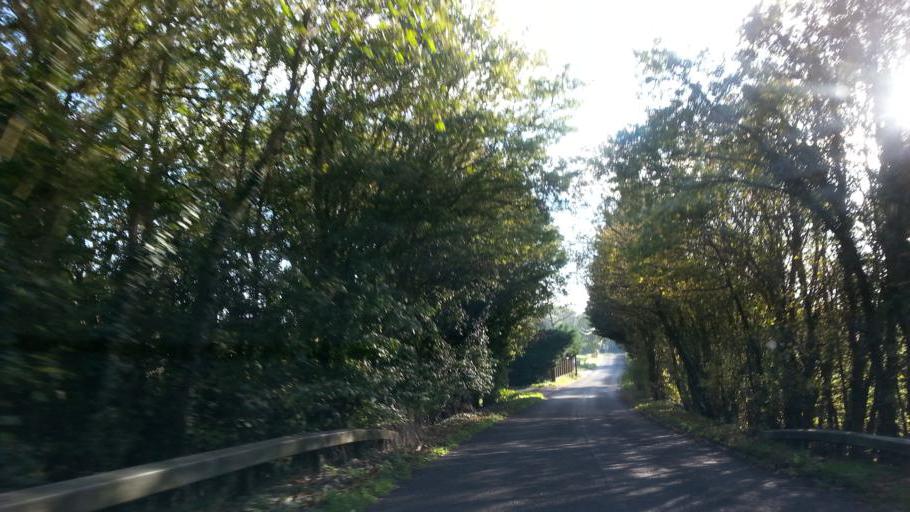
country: GB
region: England
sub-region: Suffolk
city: Thurston
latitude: 52.2359
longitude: 0.8076
